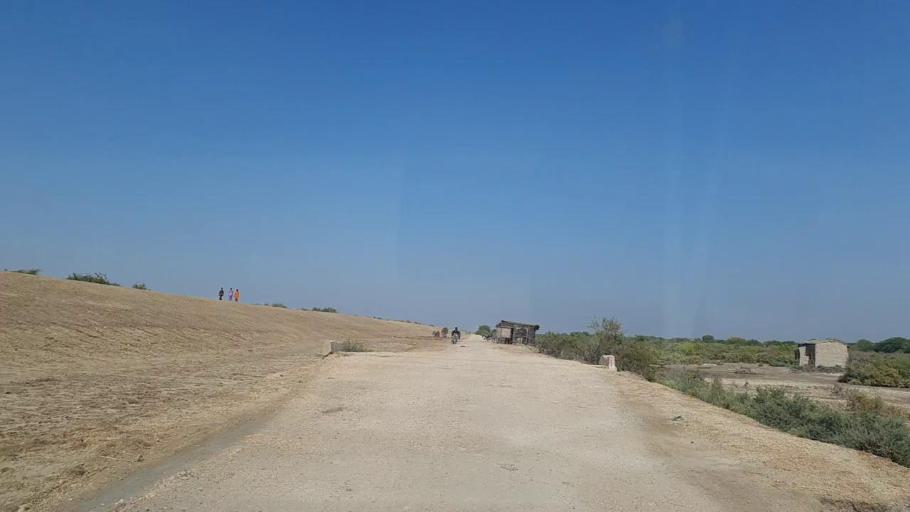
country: PK
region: Sindh
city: Chuhar Jamali
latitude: 24.4588
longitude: 68.0014
